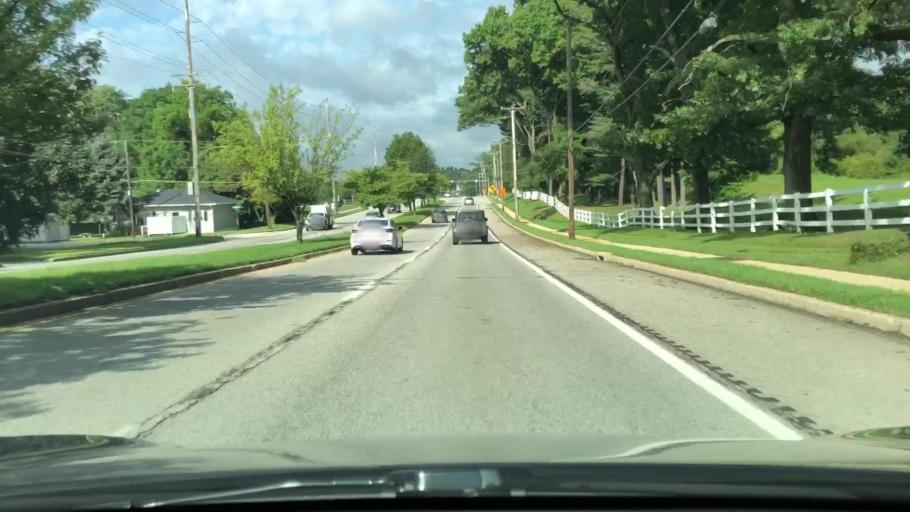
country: US
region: Pennsylvania
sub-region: Delaware County
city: Broomall
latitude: 39.9860
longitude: -75.4113
